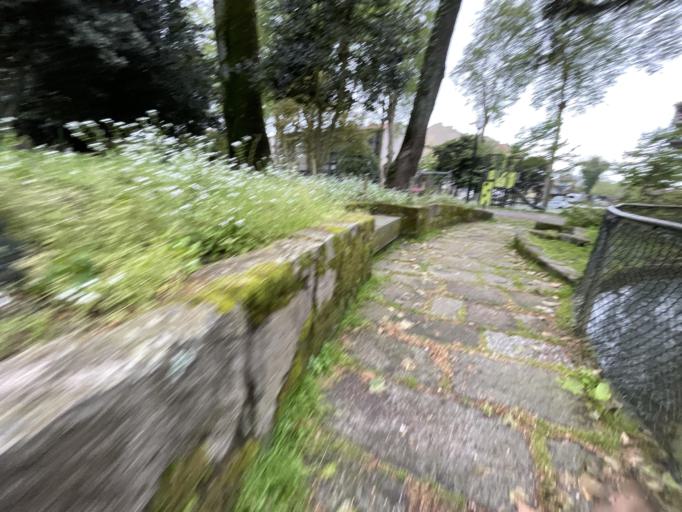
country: PT
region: Porto
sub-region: Porto
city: Porto
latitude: 41.1720
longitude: -8.6120
